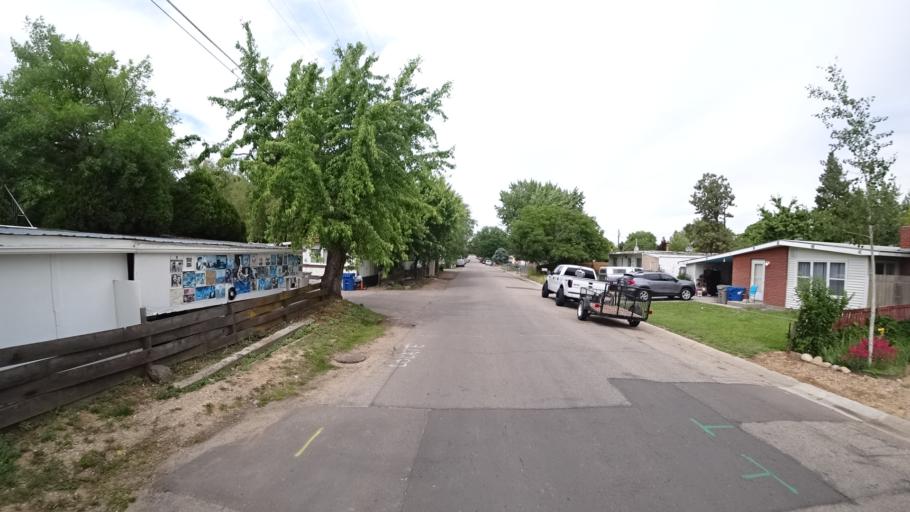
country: US
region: Idaho
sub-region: Ada County
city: Boise
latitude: 43.5790
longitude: -116.2158
